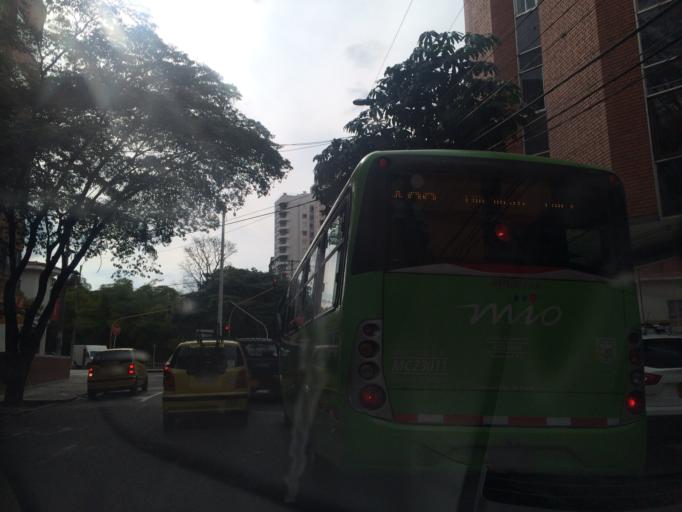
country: CO
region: Valle del Cauca
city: Cali
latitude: 3.4508
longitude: -76.5423
